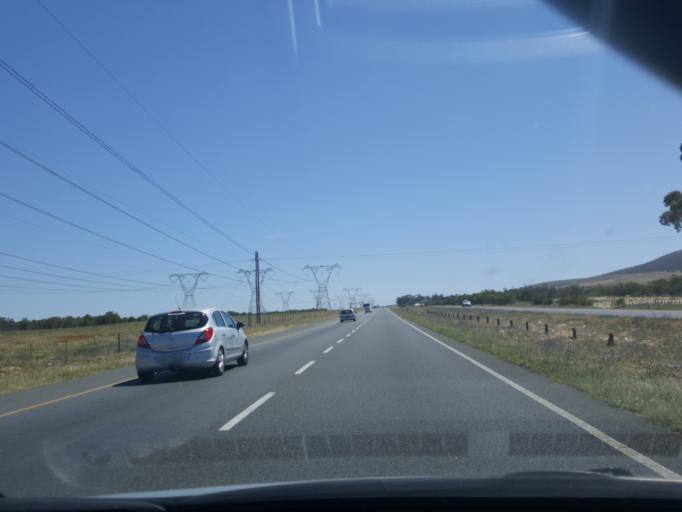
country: ZA
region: Western Cape
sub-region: City of Cape Town
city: Sunset Beach
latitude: -33.7439
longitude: 18.5457
